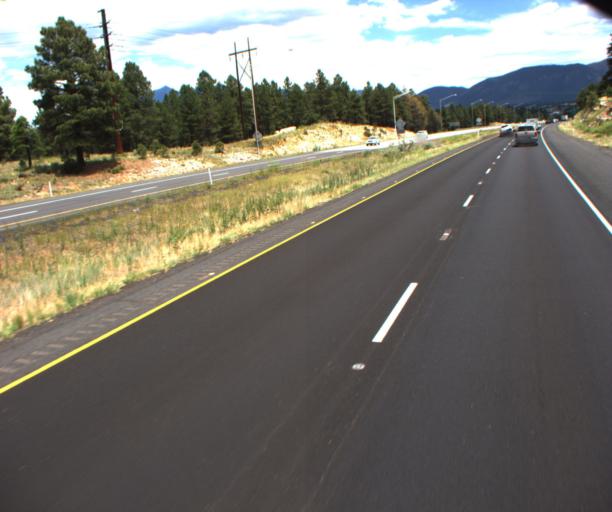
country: US
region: Arizona
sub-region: Coconino County
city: Flagstaff
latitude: 35.1595
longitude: -111.6767
